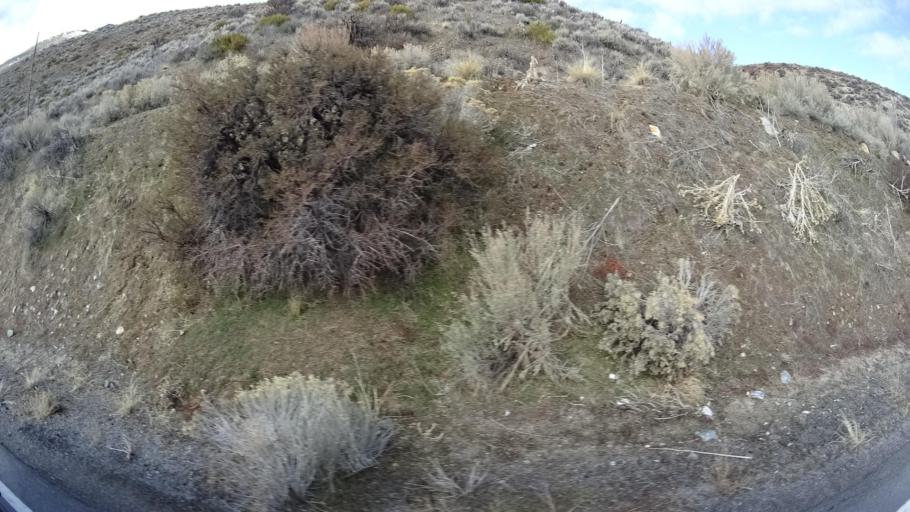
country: US
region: Nevada
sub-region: Washoe County
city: Cold Springs
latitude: 39.8256
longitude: -119.9383
